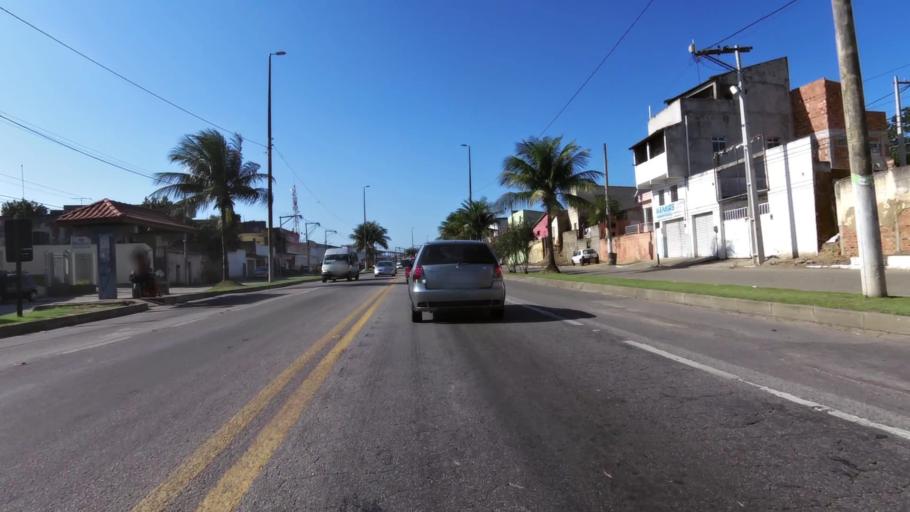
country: BR
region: Rio de Janeiro
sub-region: Campos Dos Goytacazes
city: Campos
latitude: -21.7294
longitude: -41.3228
